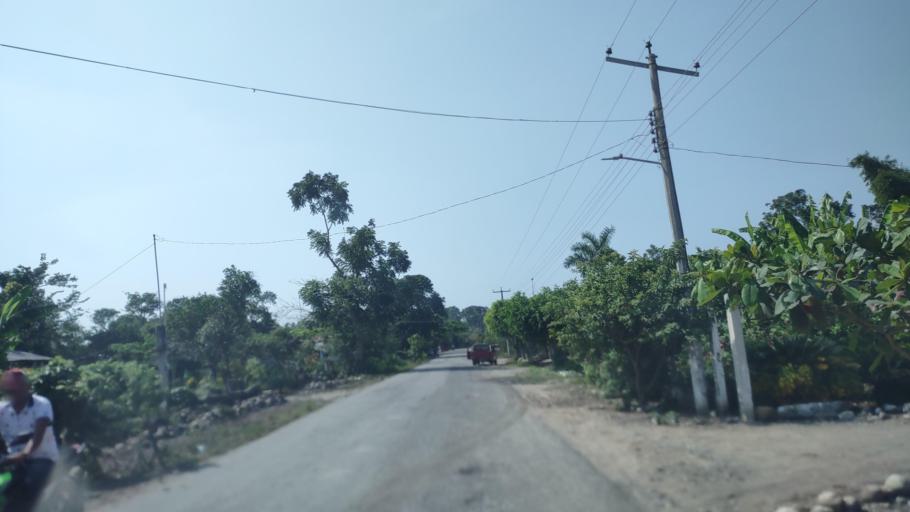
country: MX
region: Puebla
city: Espinal
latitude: 20.2554
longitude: -97.3291
